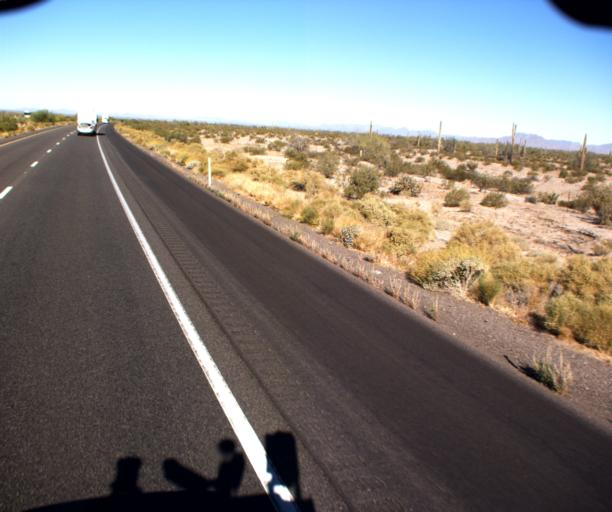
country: US
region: Arizona
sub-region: Maricopa County
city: Gila Bend
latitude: 32.9060
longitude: -112.5807
